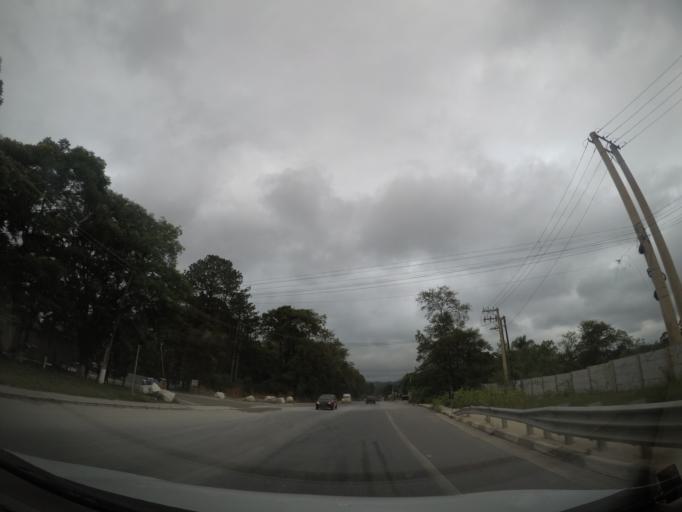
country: BR
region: Sao Paulo
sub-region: Guarulhos
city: Guarulhos
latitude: -23.3882
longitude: -46.4420
